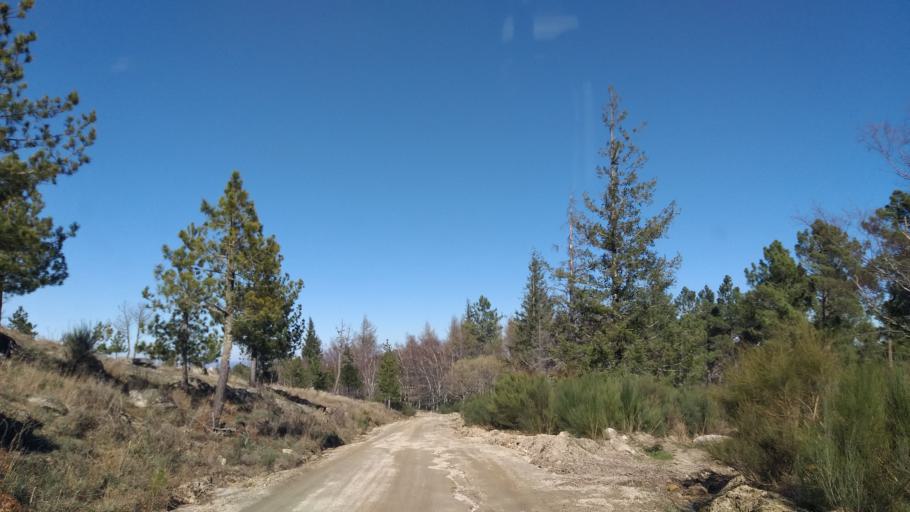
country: PT
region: Guarda
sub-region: Manteigas
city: Manteigas
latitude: 40.4930
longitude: -7.4932
